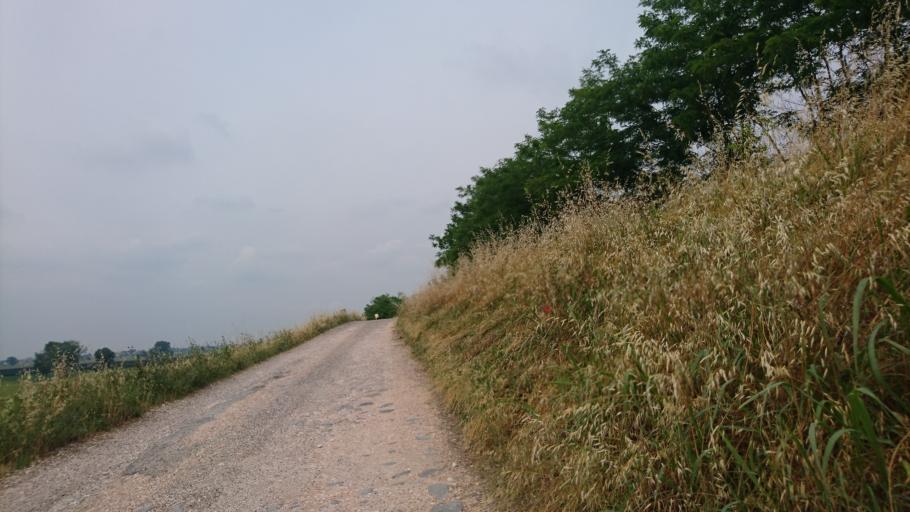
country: IT
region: Veneto
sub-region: Provincia di Rovigo
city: Lendinara
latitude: 45.1083
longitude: 11.6147
